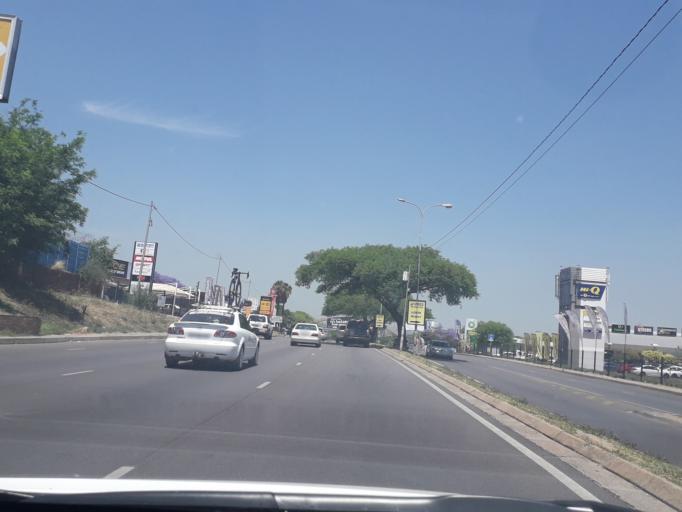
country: ZA
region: Gauteng
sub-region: City of Johannesburg Metropolitan Municipality
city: Midrand
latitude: -26.0586
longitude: 28.0231
